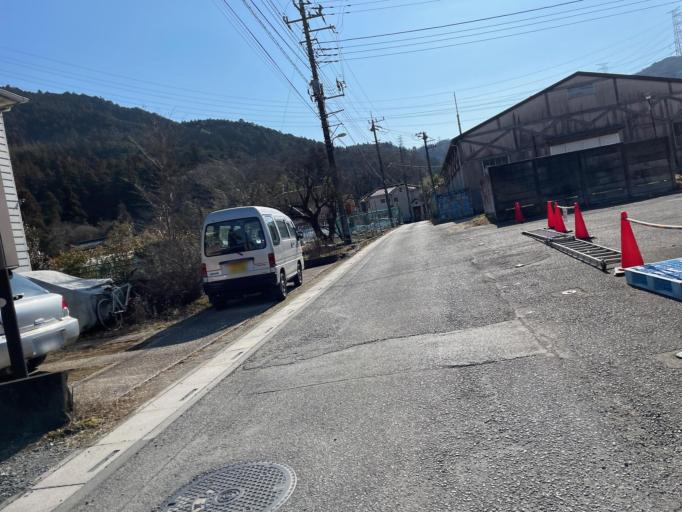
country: JP
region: Tokyo
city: Ome
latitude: 35.8660
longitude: 139.2365
